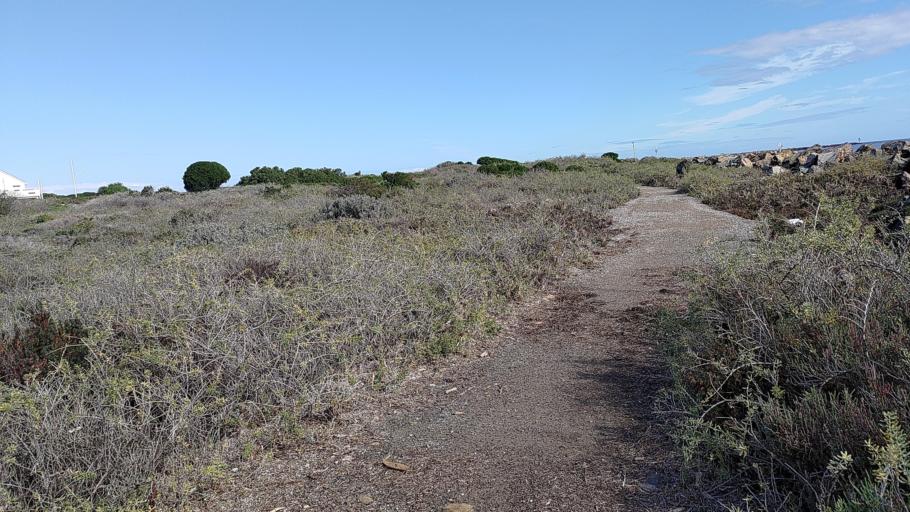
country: AU
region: South Australia
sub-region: Port Adelaide Enfield
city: Birkenhead
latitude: -34.7814
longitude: 138.4798
